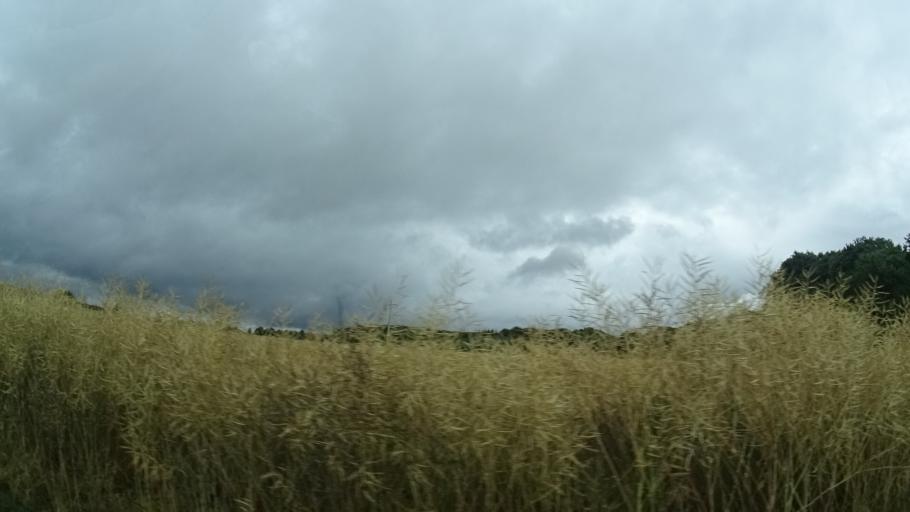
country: LU
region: Grevenmacher
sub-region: Canton de Remich
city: Dalheim
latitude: 49.5263
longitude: 6.2607
